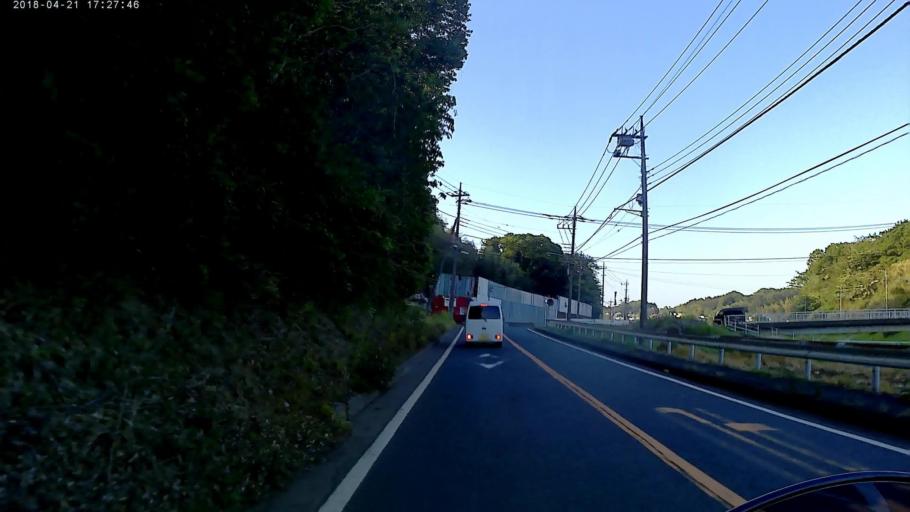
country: JP
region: Kanagawa
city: Atsugi
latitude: 35.4185
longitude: 139.4123
